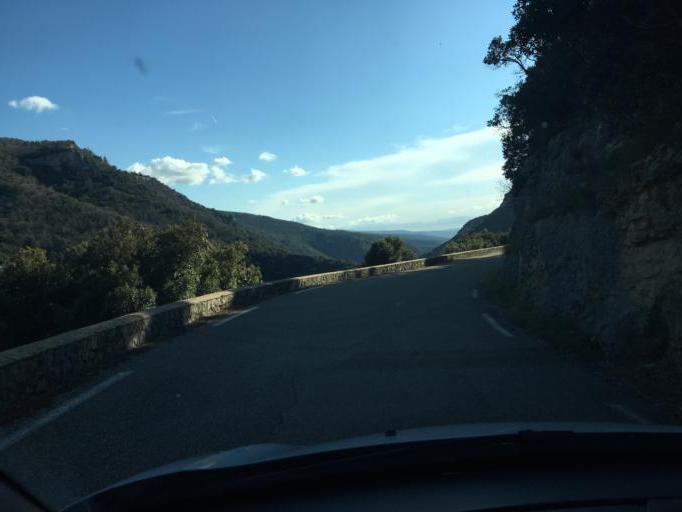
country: FR
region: Provence-Alpes-Cote d'Azur
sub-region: Departement du Vaucluse
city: Villes-sur-Auzon
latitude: 44.0668
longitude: 5.3098
